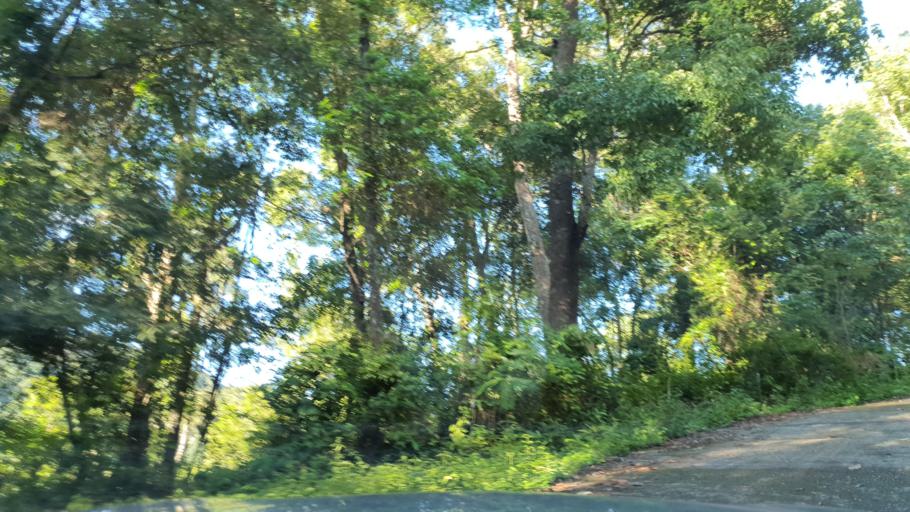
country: TH
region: Chiang Mai
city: Mae On
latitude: 18.8157
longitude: 99.3506
